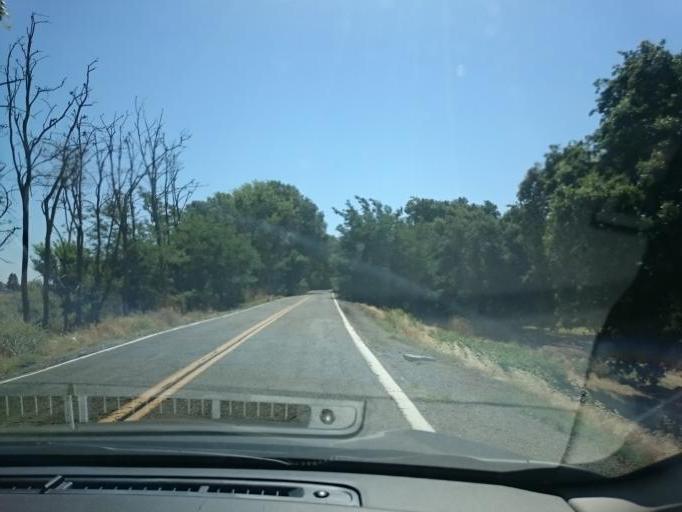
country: US
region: California
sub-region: Sacramento County
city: Parkway
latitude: 38.4732
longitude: -121.5198
